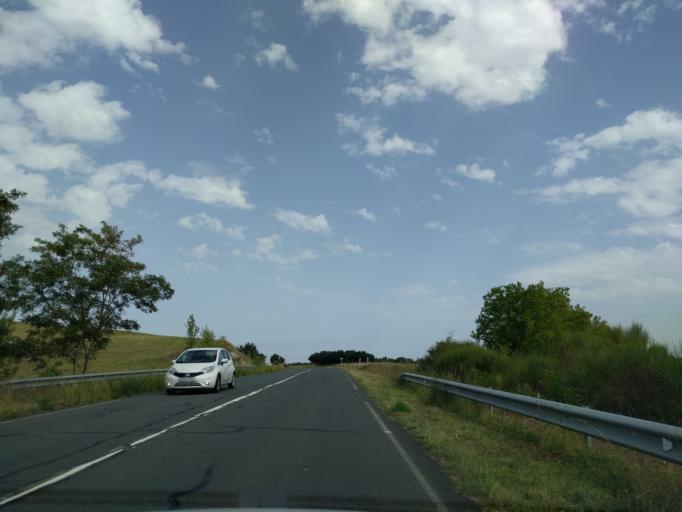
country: FR
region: Midi-Pyrenees
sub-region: Departement du Tarn
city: Saix
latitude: 43.6481
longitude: 2.1851
